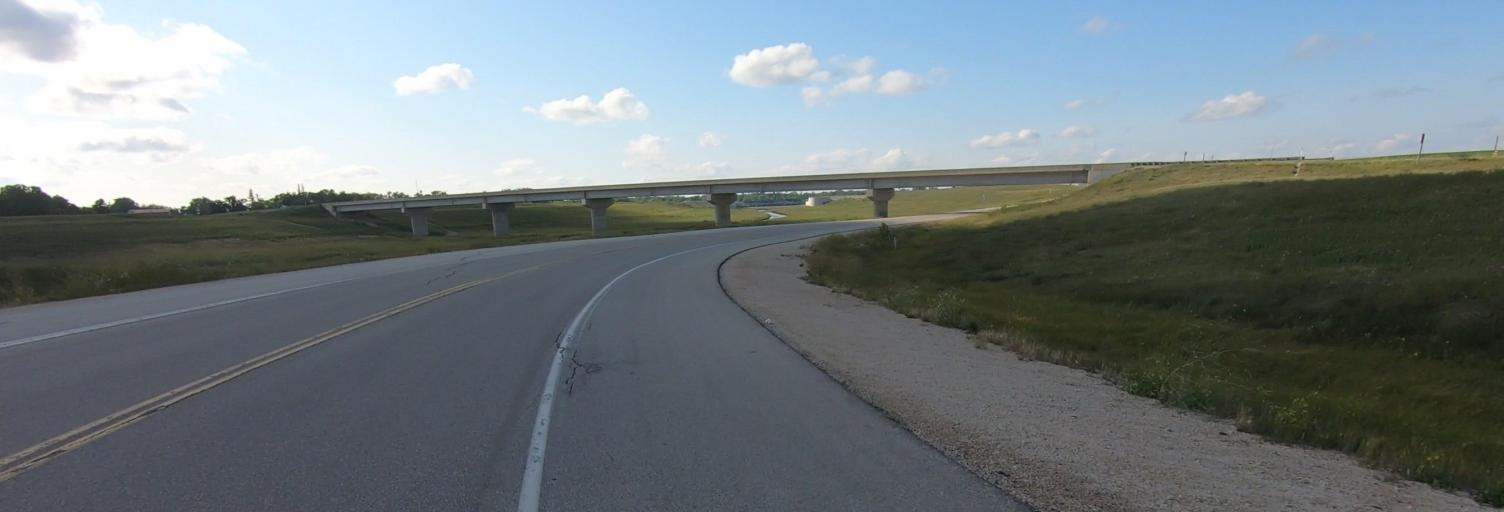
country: CA
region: Manitoba
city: Selkirk
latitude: 50.0842
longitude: -96.9247
